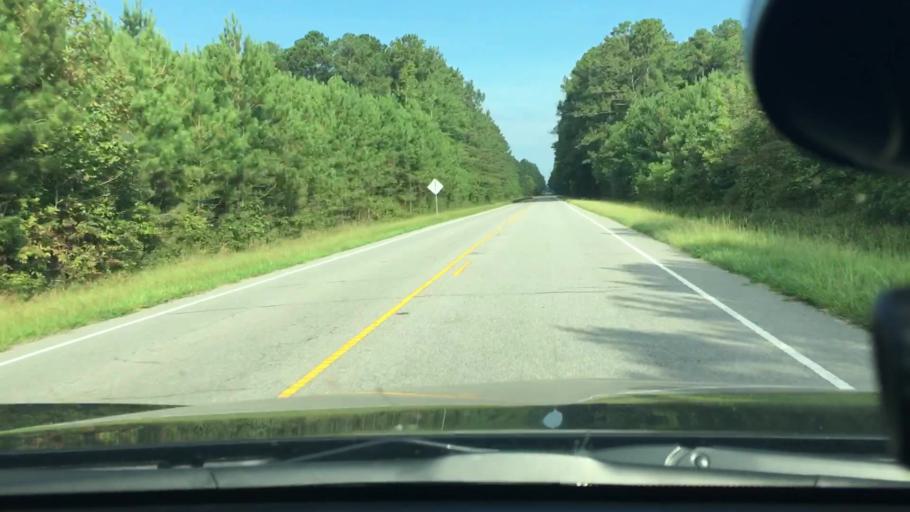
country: US
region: North Carolina
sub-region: Edgecombe County
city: Pinetops
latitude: 35.7622
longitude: -77.5591
